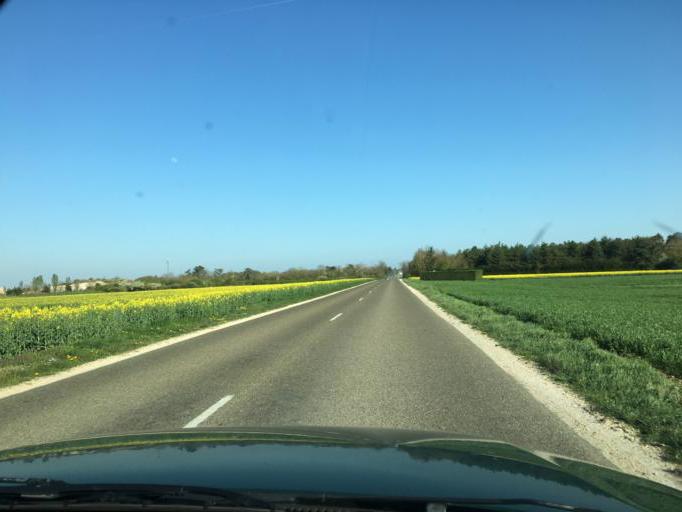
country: FR
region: Centre
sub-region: Departement du Loiret
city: Baule
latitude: 47.8496
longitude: 1.6319
